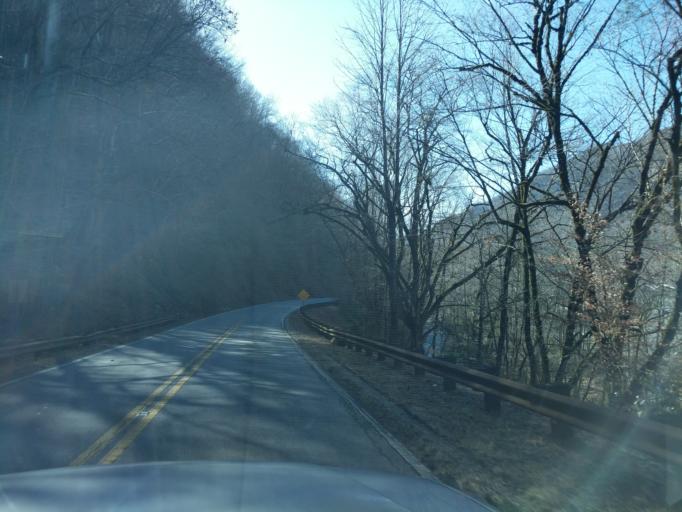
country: US
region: North Carolina
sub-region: Graham County
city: Robbinsville
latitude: 35.3096
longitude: -83.6438
